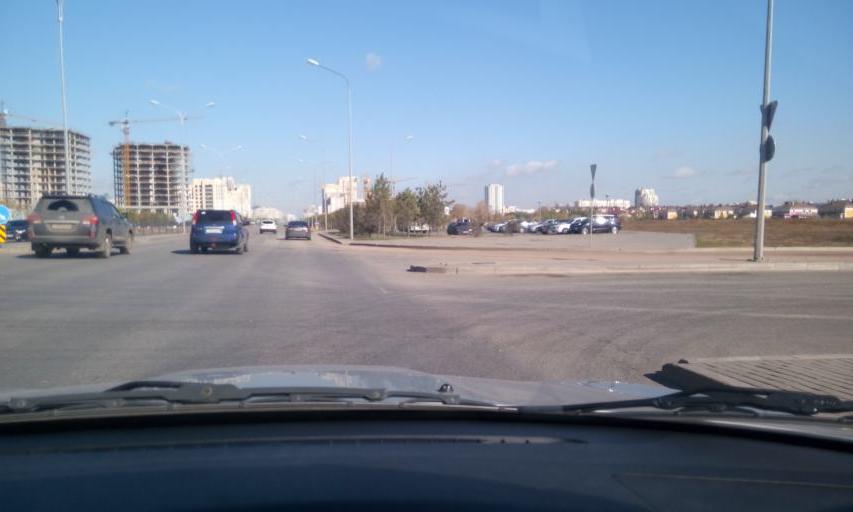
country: KZ
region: Astana Qalasy
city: Astana
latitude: 51.0865
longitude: 71.4238
